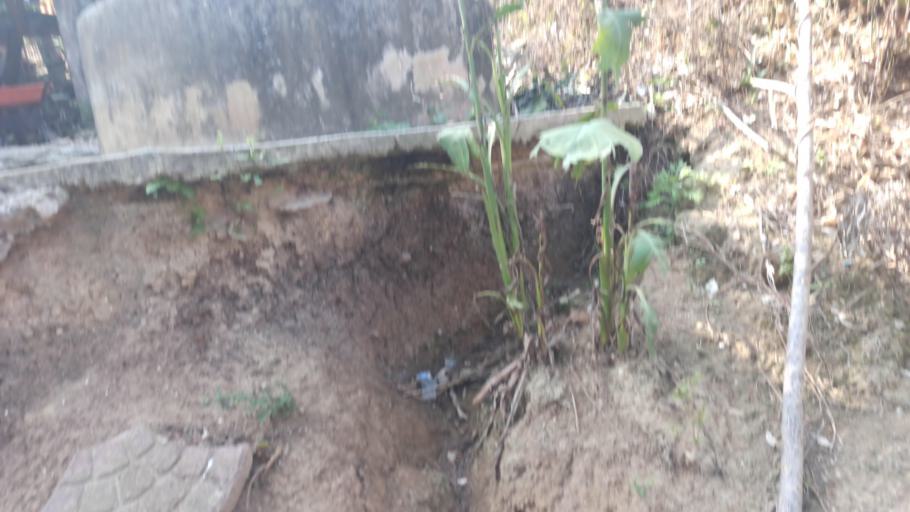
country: MX
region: Veracruz
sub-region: Cazones de Herrera
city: Rancho Nuevo
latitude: 20.6212
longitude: -97.2176
